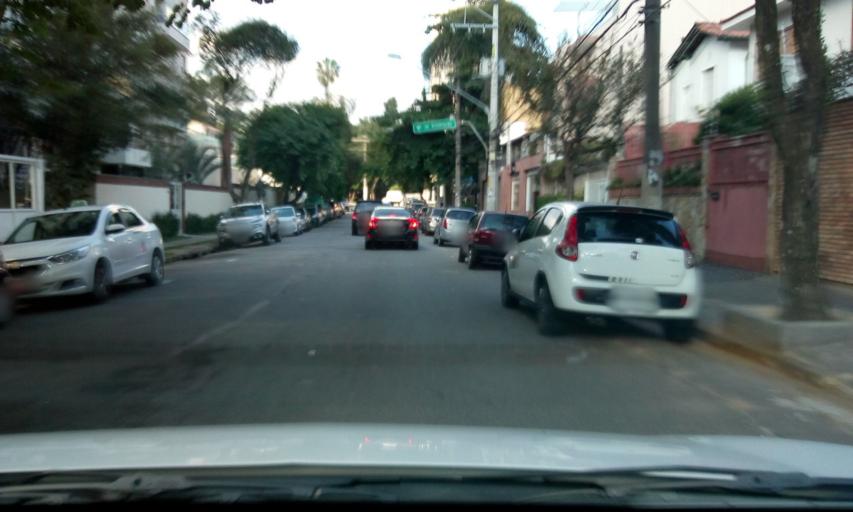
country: BR
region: Sao Paulo
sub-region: Sao Paulo
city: Sao Paulo
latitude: -23.5739
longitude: -46.6324
